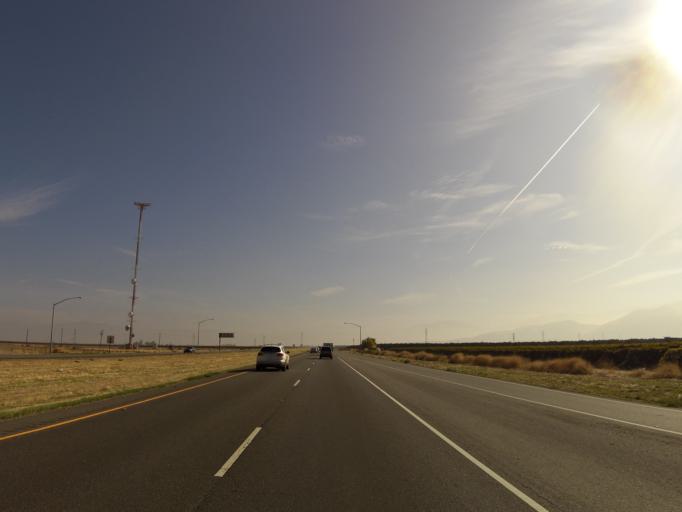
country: US
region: California
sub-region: Kern County
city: Weedpatch
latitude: 35.0575
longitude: -118.9975
